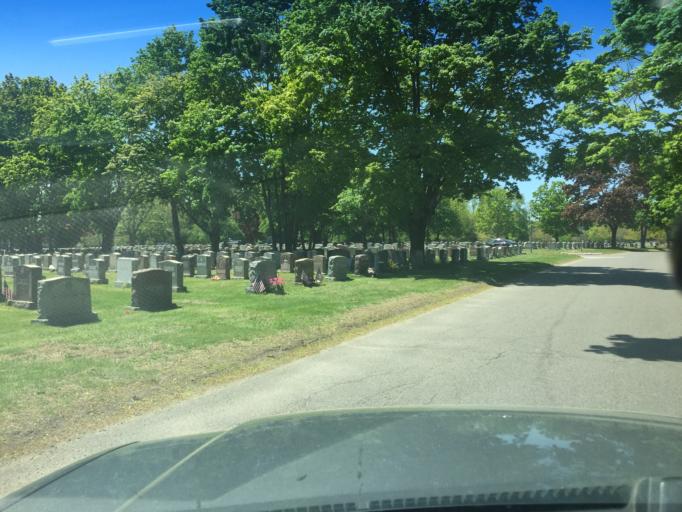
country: US
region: Massachusetts
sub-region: Middlesex County
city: Winchester
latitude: 42.4292
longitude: -71.1359
